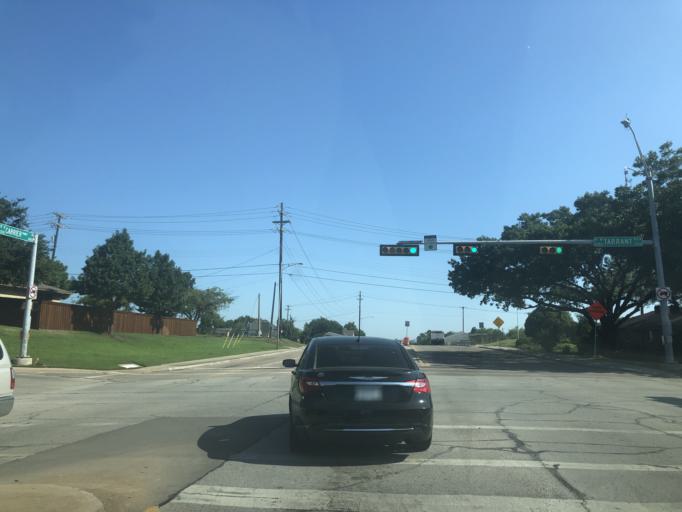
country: US
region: Texas
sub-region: Dallas County
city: Grand Prairie
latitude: 32.7582
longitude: -97.0198
